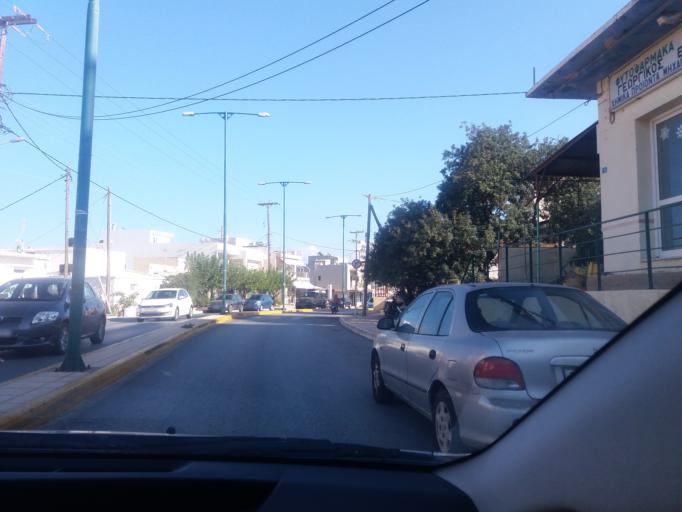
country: GR
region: Crete
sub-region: Nomos Lasithiou
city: Agios Nikolaos
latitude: 35.1977
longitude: 25.7101
